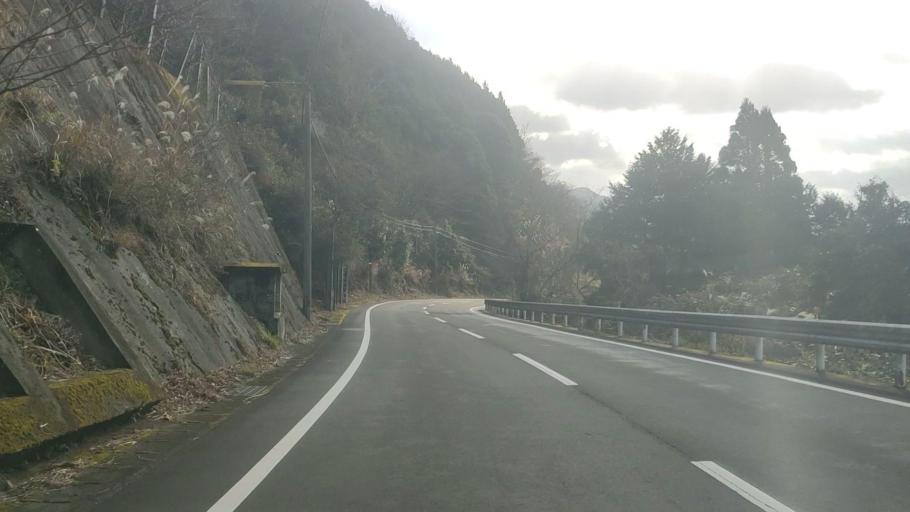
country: JP
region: Kumamoto
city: Hitoyoshi
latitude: 32.3208
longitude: 130.8409
